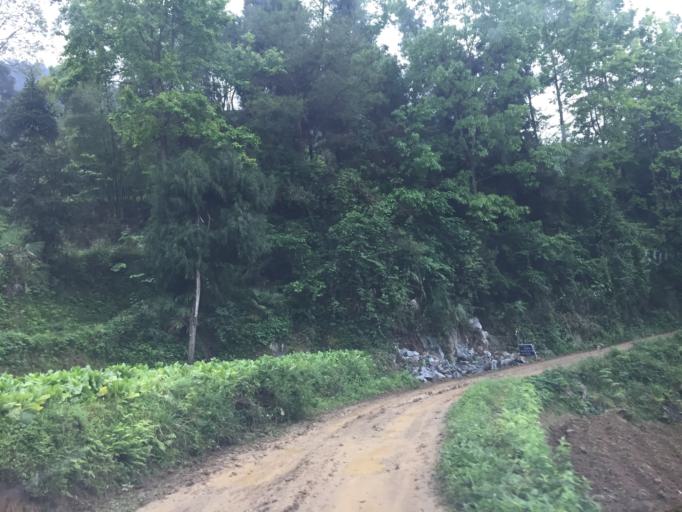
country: CN
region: Guizhou Sheng
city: Kuanping
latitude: 28.0227
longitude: 108.0643
